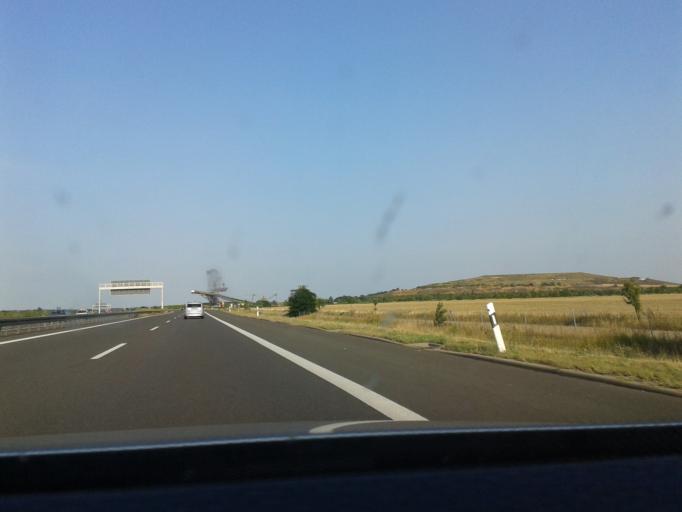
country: DE
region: Saxony
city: Markkleeberg
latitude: 51.2477
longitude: 12.4089
